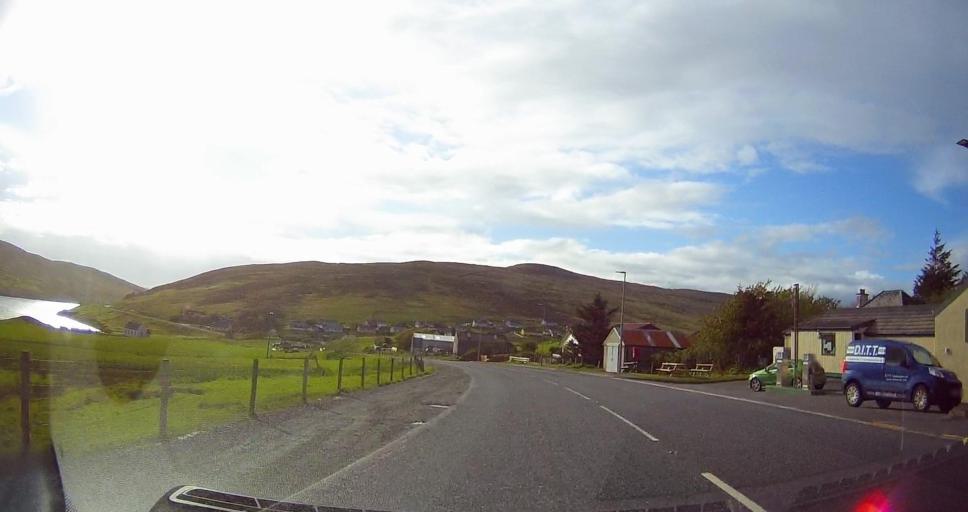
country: GB
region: Scotland
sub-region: Shetland Islands
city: Lerwick
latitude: 60.3552
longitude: -1.2621
